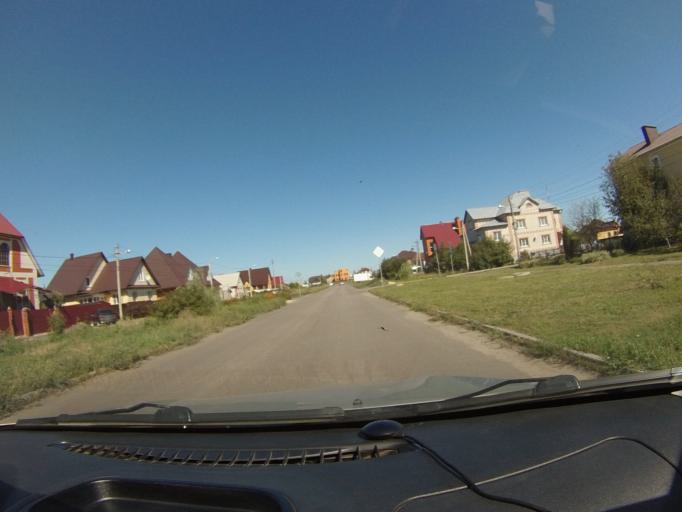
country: RU
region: Tambov
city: Tambov
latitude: 52.7801
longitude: 41.3844
